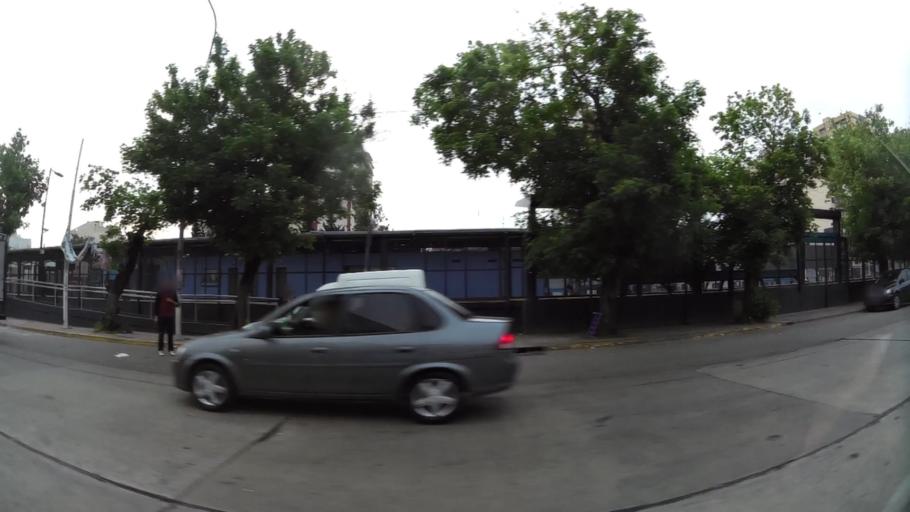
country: AR
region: Buenos Aires
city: San Justo
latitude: -34.6402
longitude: -58.5406
